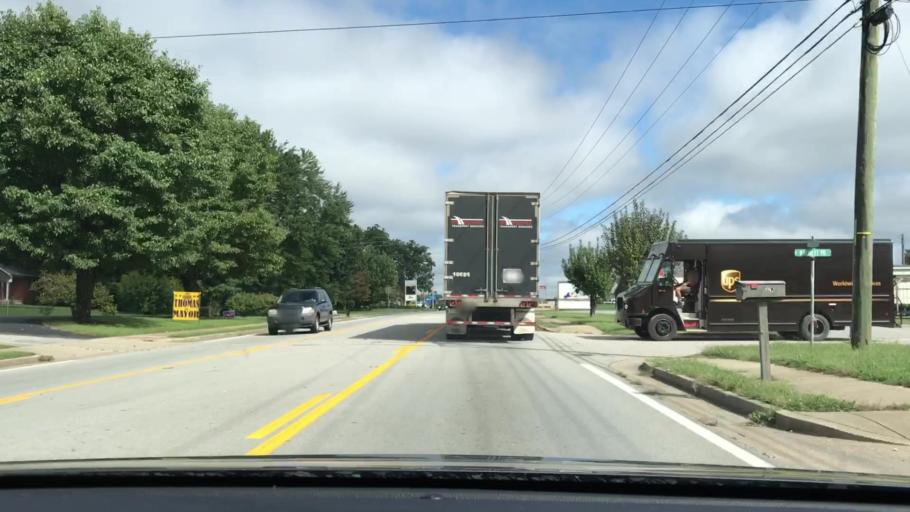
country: US
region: Kentucky
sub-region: Russell County
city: Russell Springs
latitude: 37.0314
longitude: -85.0766
